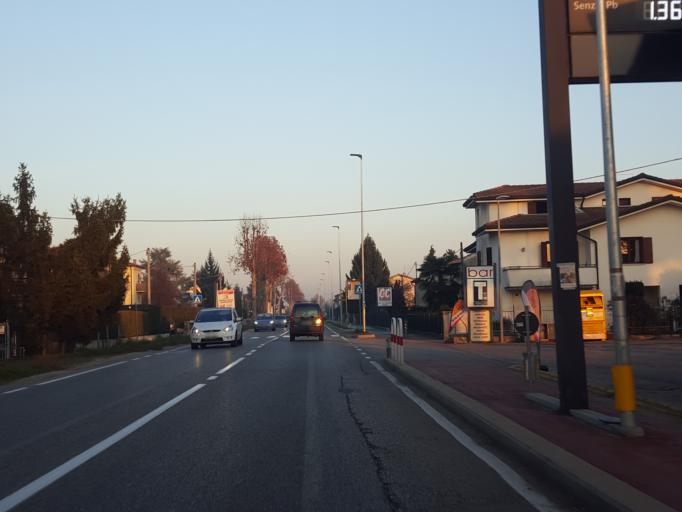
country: IT
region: Veneto
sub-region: Provincia di Vicenza
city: Monticello Conte Otto
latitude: 45.5726
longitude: 11.5817
